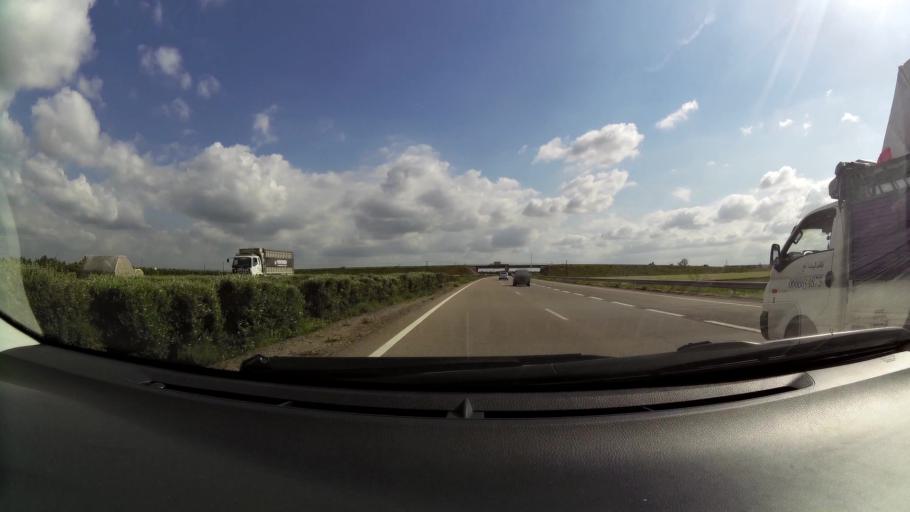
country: MA
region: Chaouia-Ouardigha
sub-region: Settat Province
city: Berrechid
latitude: 33.2739
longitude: -7.5477
